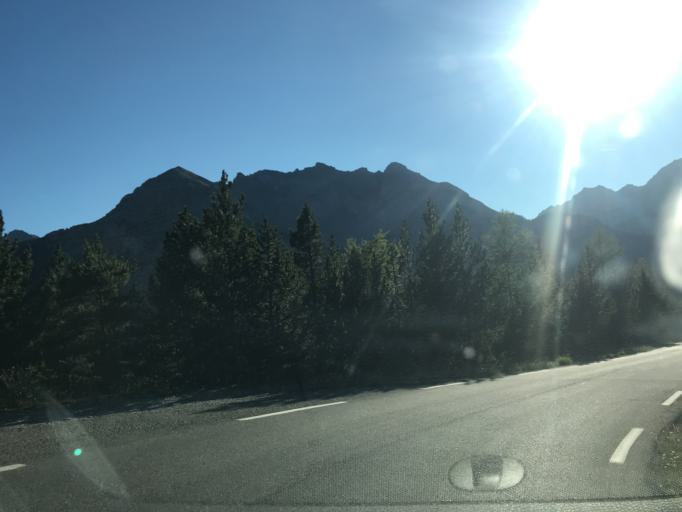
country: FR
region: Provence-Alpes-Cote d'Azur
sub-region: Departement des Hautes-Alpes
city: Villar-Saint-Pancrace
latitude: 44.7994
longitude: 6.7321
